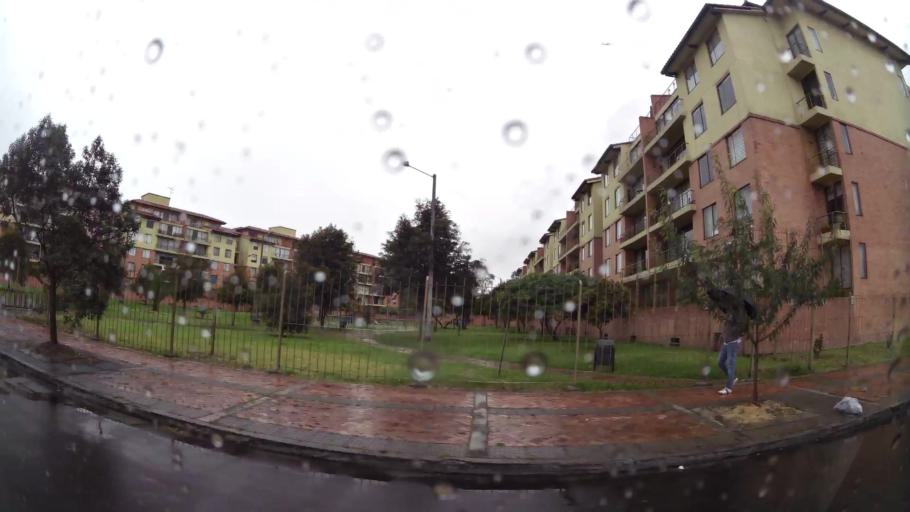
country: CO
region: Bogota D.C.
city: Bogota
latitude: 4.6614
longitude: -74.1206
